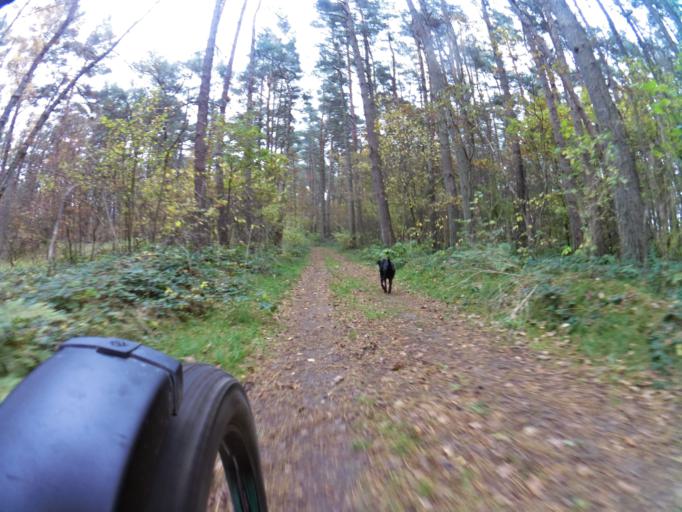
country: PL
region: Pomeranian Voivodeship
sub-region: Powiat pucki
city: Krokowa
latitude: 54.8296
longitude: 18.1232
